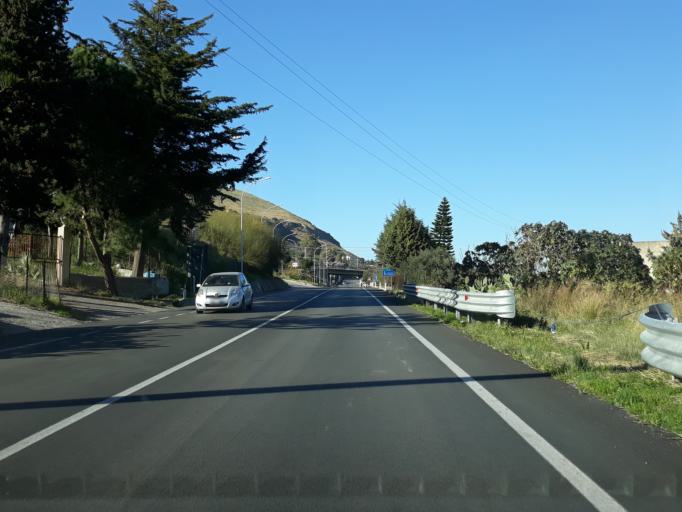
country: IT
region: Sicily
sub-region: Palermo
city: Misilmeri
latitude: 38.0409
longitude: 13.4610
